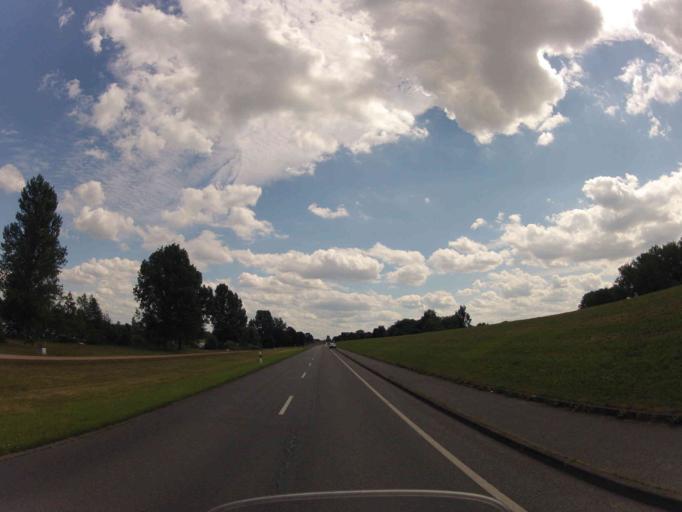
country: DE
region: Lower Saxony
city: Stelle
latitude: 53.4343
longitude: 10.1107
